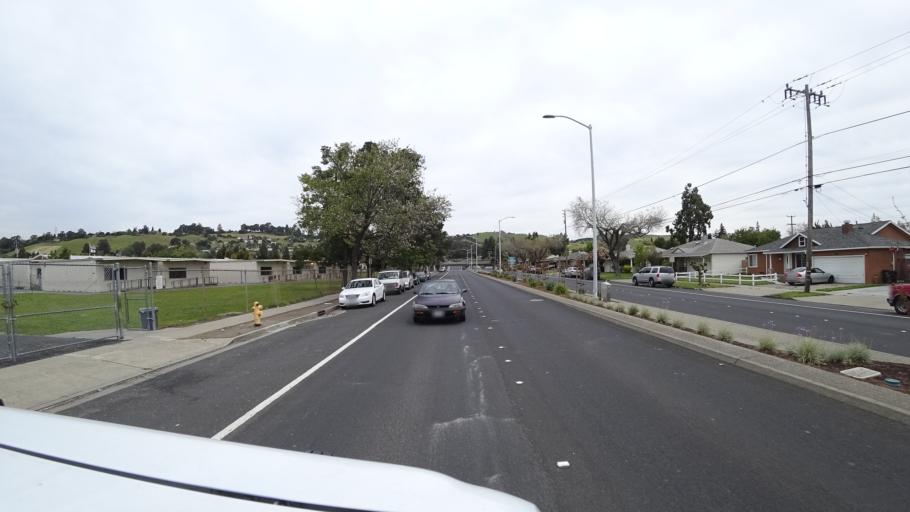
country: US
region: California
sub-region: Alameda County
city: Hayward
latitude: 37.6501
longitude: -122.0731
